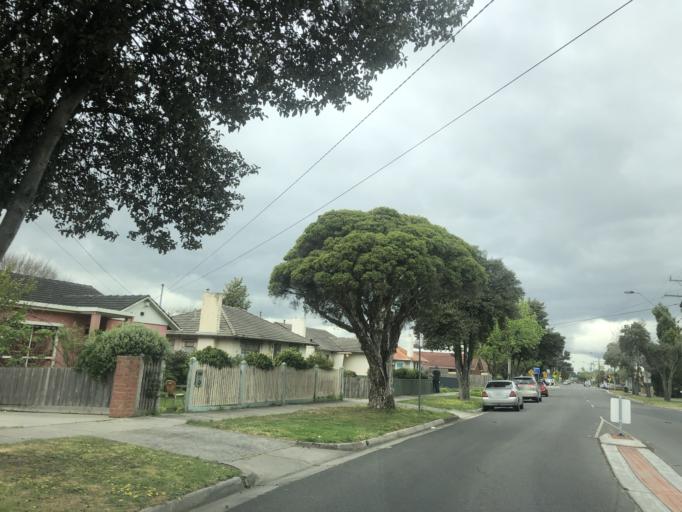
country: AU
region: Victoria
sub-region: Greater Dandenong
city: Dandenong North
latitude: -37.9647
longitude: 145.2079
